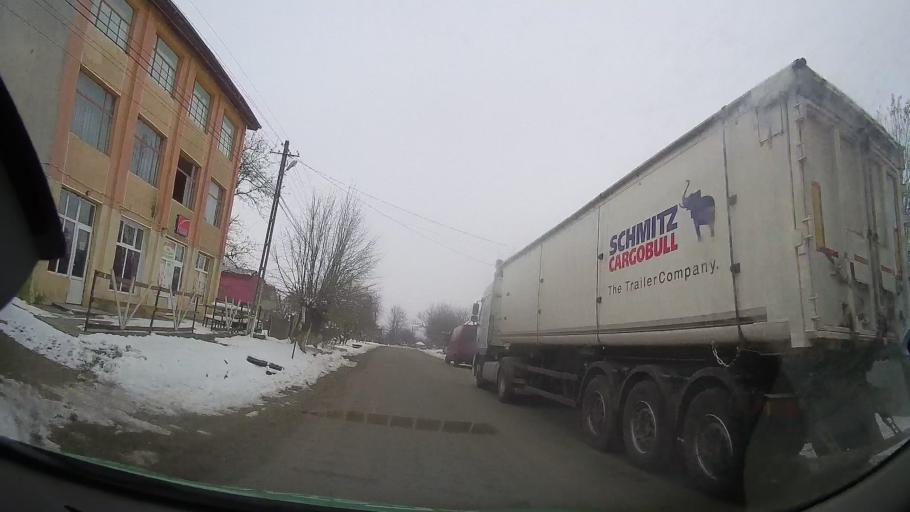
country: RO
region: Bacau
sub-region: Comuna Vultureni
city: Vultureni
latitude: 46.4034
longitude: 27.2731
